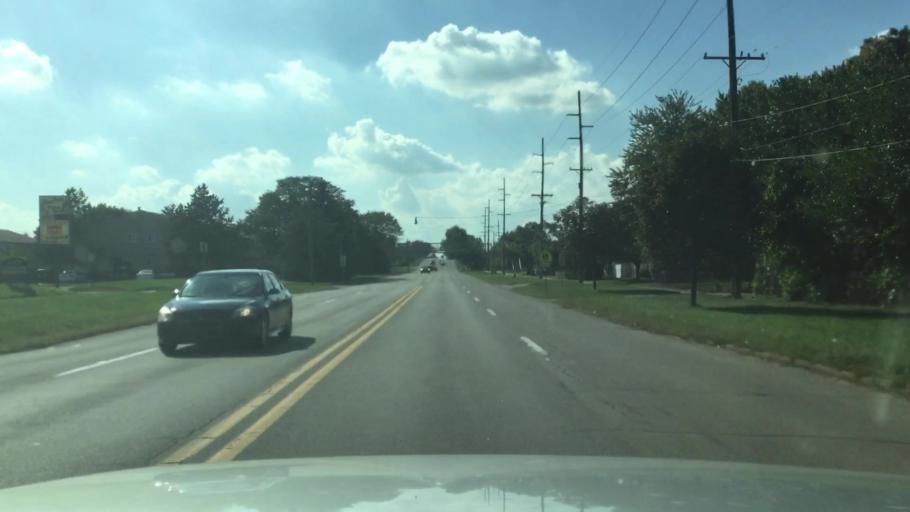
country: US
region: Michigan
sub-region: Wayne County
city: Westland
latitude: 42.3525
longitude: -83.4309
